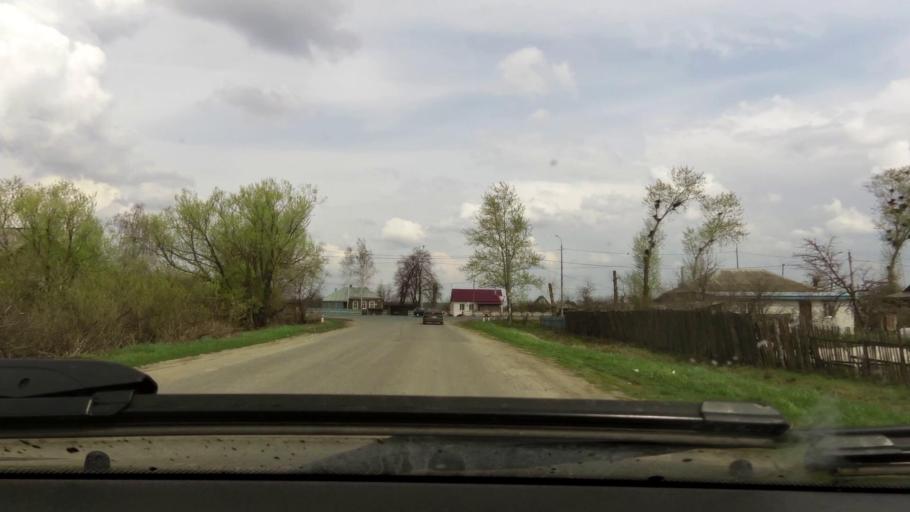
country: RU
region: Rjazan
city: Bagramovo
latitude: 54.7507
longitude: 39.4224
